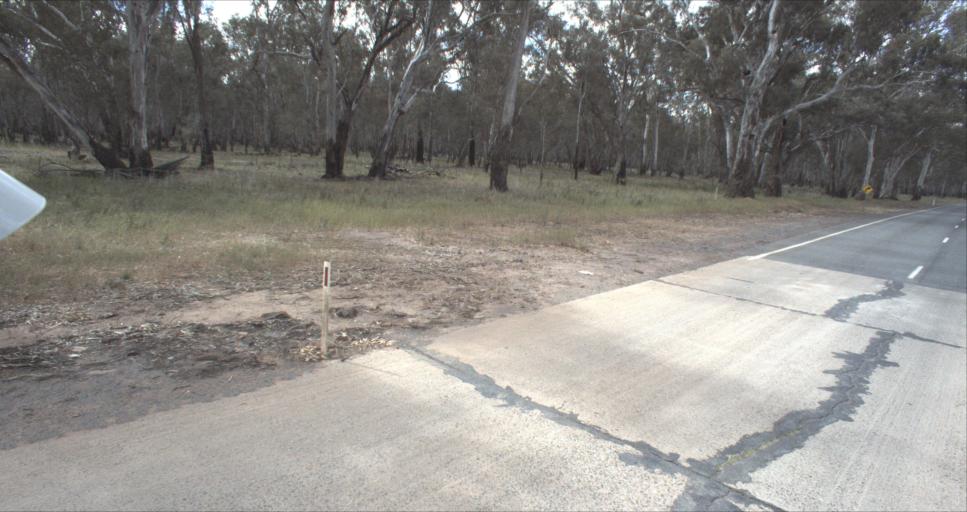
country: AU
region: New South Wales
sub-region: Leeton
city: Leeton
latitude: -34.6425
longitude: 146.3576
